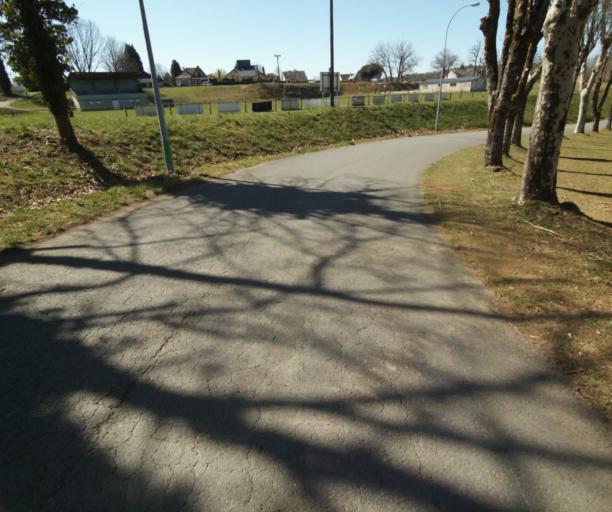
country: FR
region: Limousin
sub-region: Departement de la Correze
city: Seilhac
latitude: 45.3758
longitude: 1.6995
